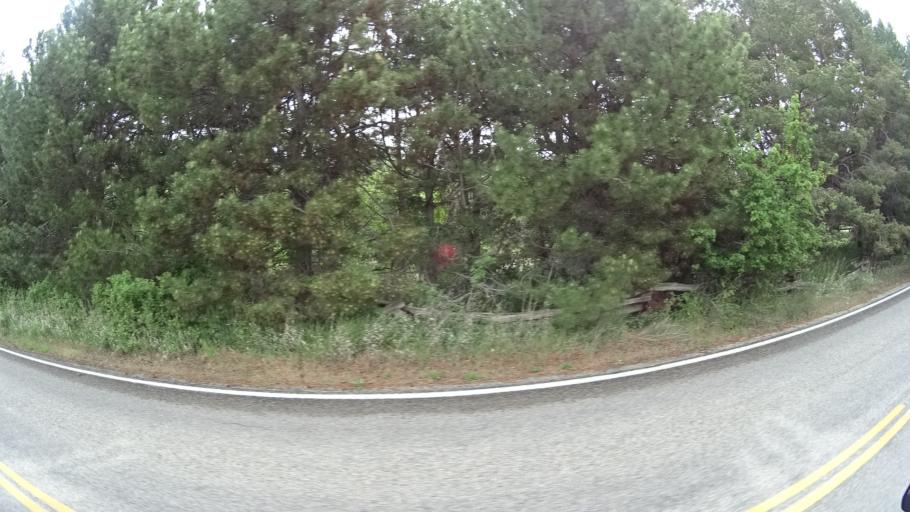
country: US
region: Idaho
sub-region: Ada County
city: Eagle
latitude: 43.7341
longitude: -116.3570
